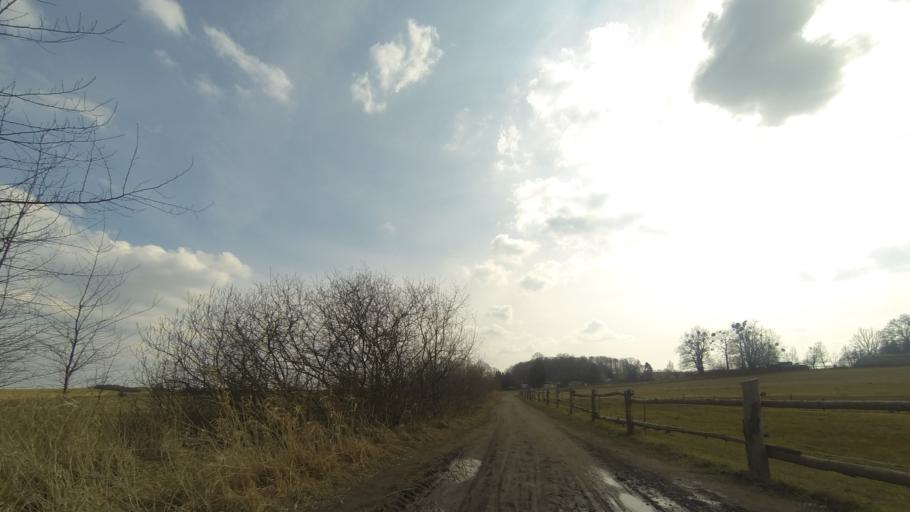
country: DE
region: Saxony
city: Moritzburg
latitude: 51.1628
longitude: 13.7131
